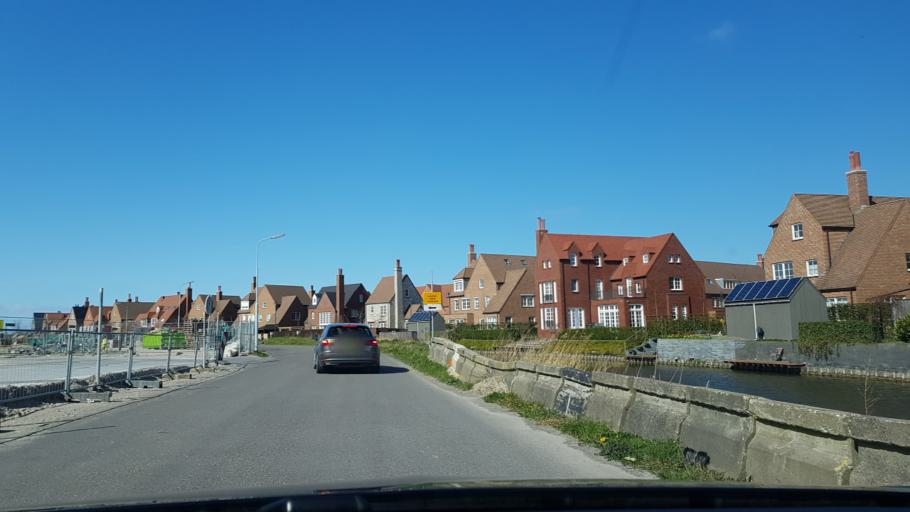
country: NL
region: North Holland
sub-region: Gemeente Haarlemmermeer
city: Hoofddorp
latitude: 52.2921
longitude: 4.6593
